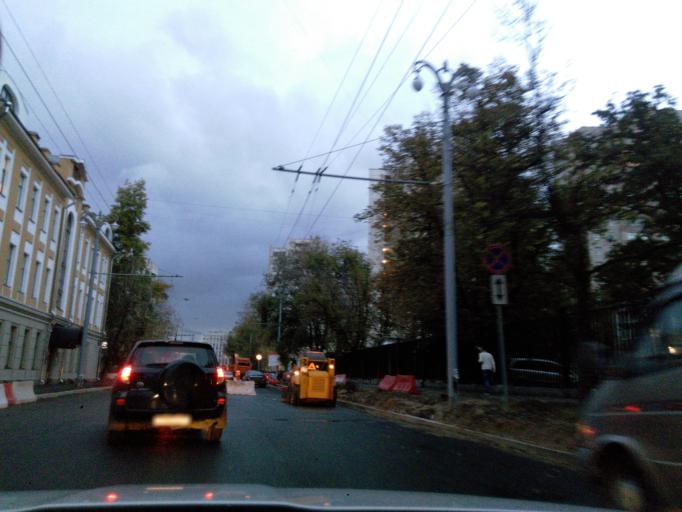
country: RU
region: Moscow
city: Zamoskvorech'ye
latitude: 55.7264
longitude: 37.6154
